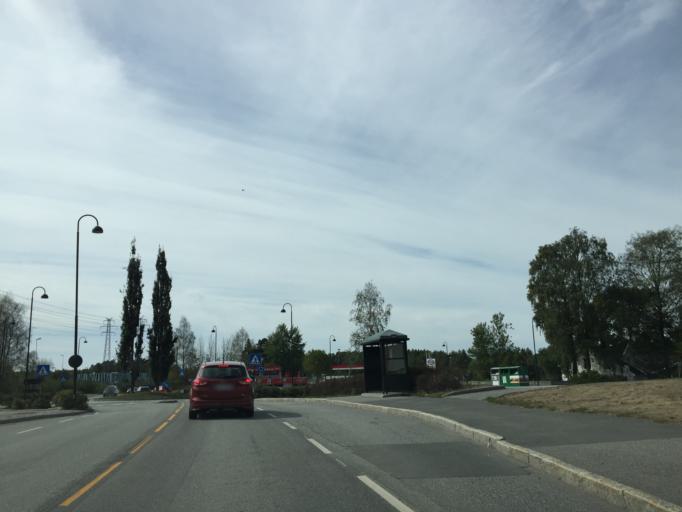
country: NO
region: Ostfold
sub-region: Moss
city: Moss
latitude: 59.4469
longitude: 10.6862
